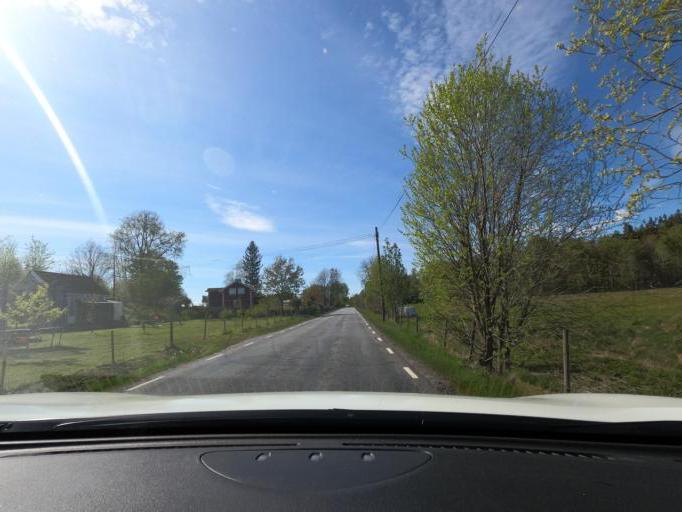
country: SE
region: Vaestra Goetaland
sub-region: Marks Kommun
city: Kinna
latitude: 57.4758
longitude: 12.5744
